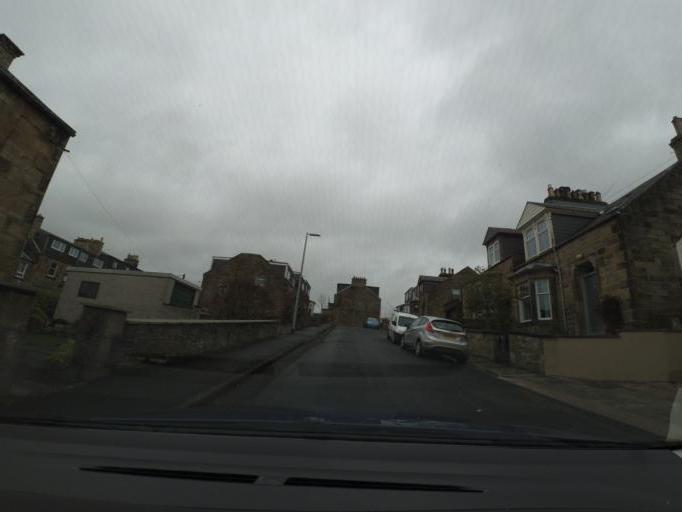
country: GB
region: Scotland
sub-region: The Scottish Borders
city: Hawick
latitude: 55.4227
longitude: -2.7820
